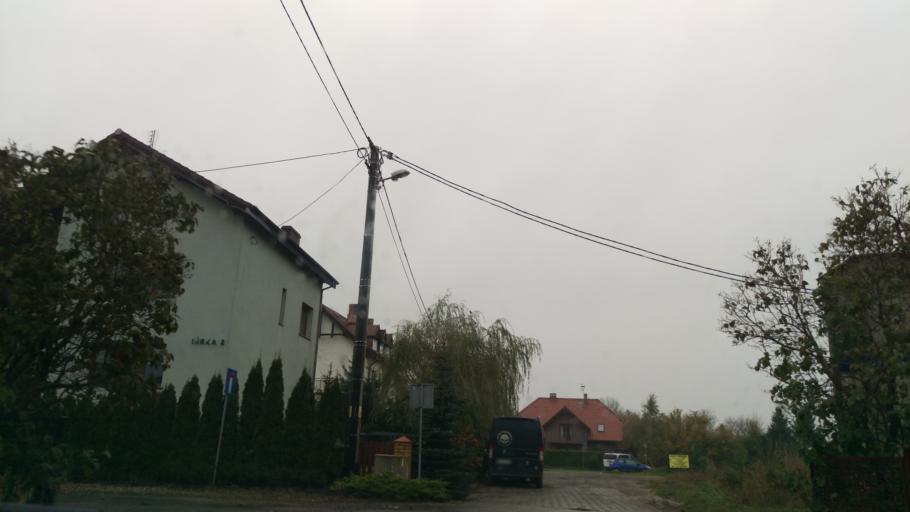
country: PL
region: West Pomeranian Voivodeship
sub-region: Szczecin
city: Szczecin
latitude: 53.4059
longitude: 14.6911
